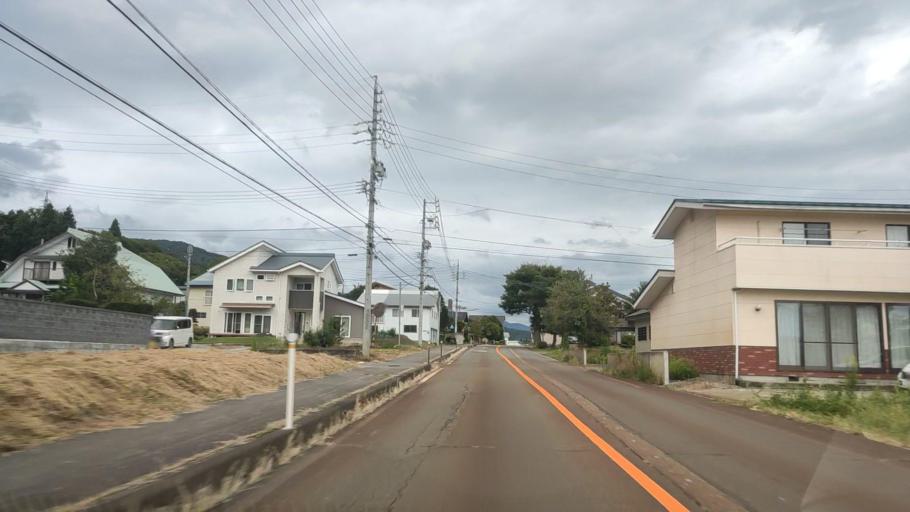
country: JP
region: Nagano
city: Iiyama
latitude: 36.8147
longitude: 138.3491
